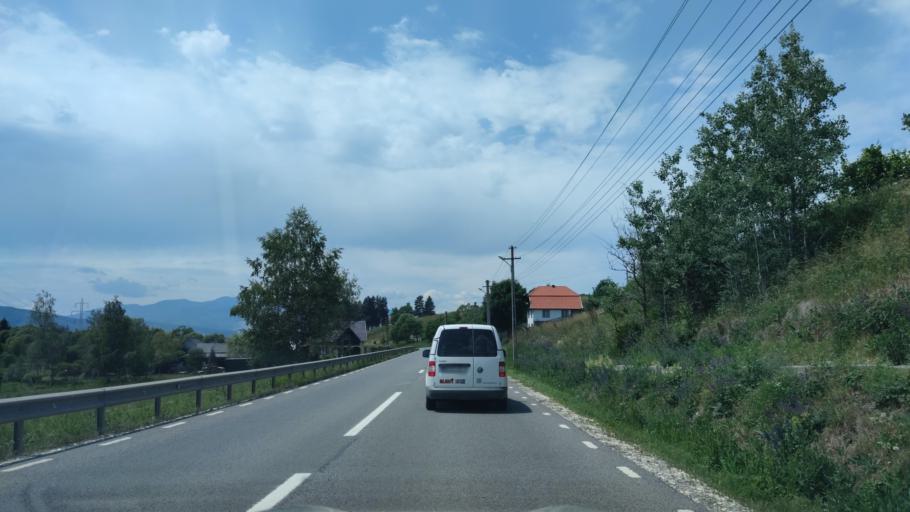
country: RO
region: Harghita
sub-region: Comuna Voslobeni
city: Voslobeni
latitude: 46.6282
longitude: 25.6725
